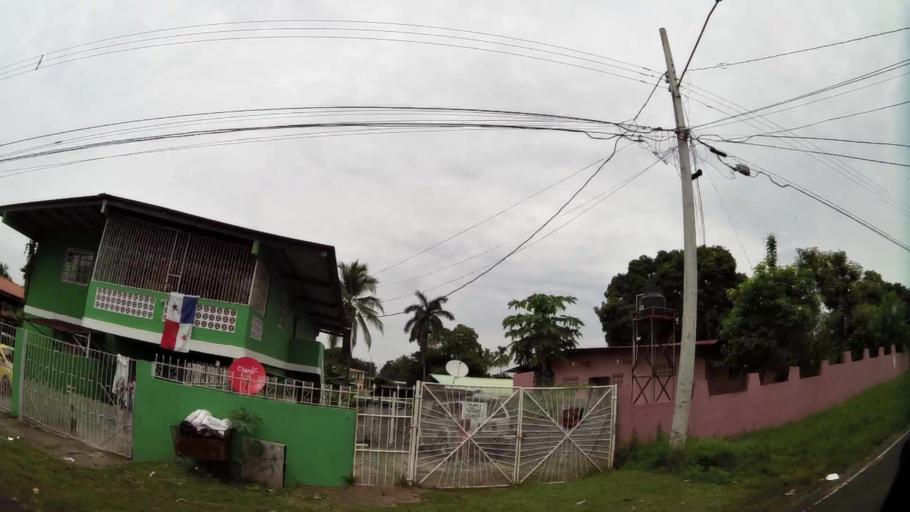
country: PA
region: Panama
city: San Miguelito
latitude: 9.0442
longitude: -79.4358
